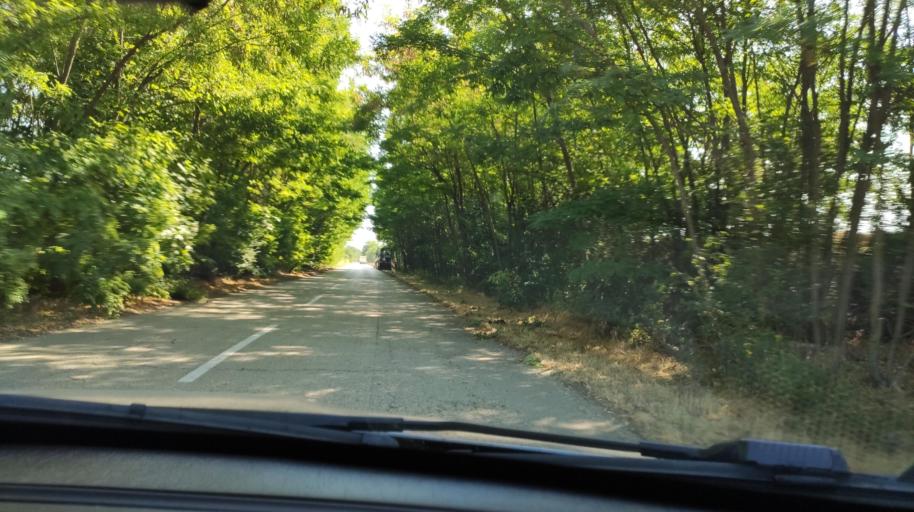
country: RS
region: Autonomna Pokrajina Vojvodina
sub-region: Severnobacki Okrug
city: Backa Topola
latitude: 45.8640
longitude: 19.6014
